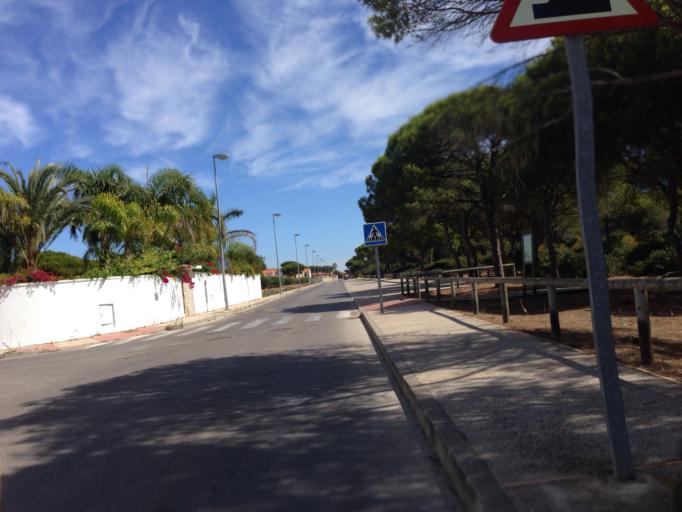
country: ES
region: Andalusia
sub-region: Provincia de Cadiz
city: Chiclana de la Frontera
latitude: 36.3776
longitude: -6.1950
